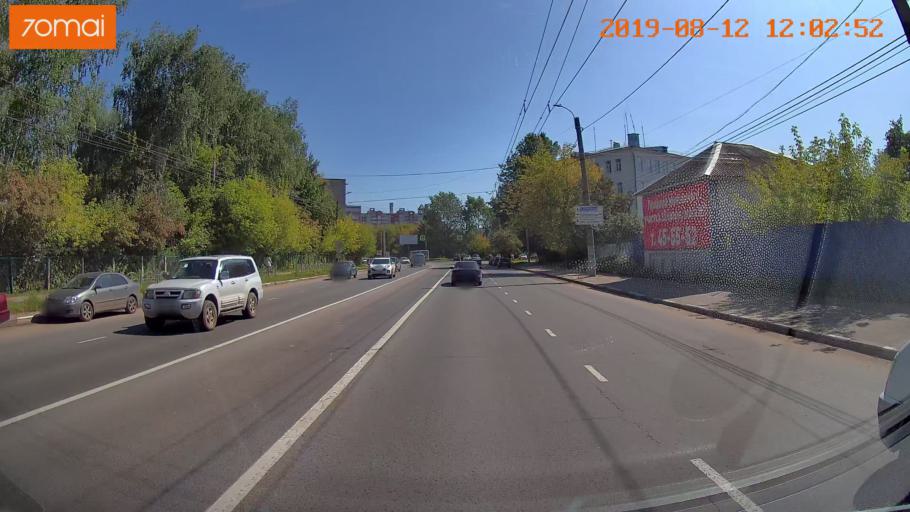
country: RU
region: Ivanovo
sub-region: Gorod Ivanovo
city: Ivanovo
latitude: 56.9953
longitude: 40.9950
